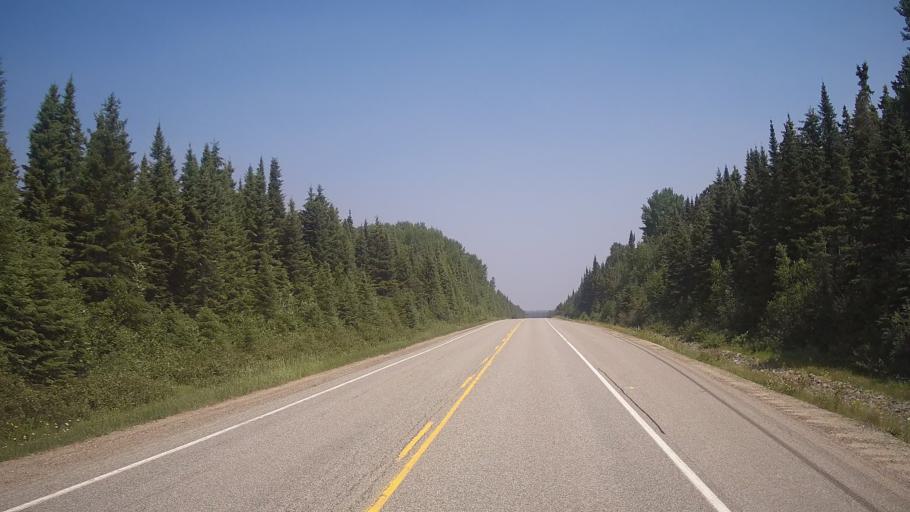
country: CA
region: Ontario
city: Timmins
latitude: 48.2011
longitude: -81.5792
